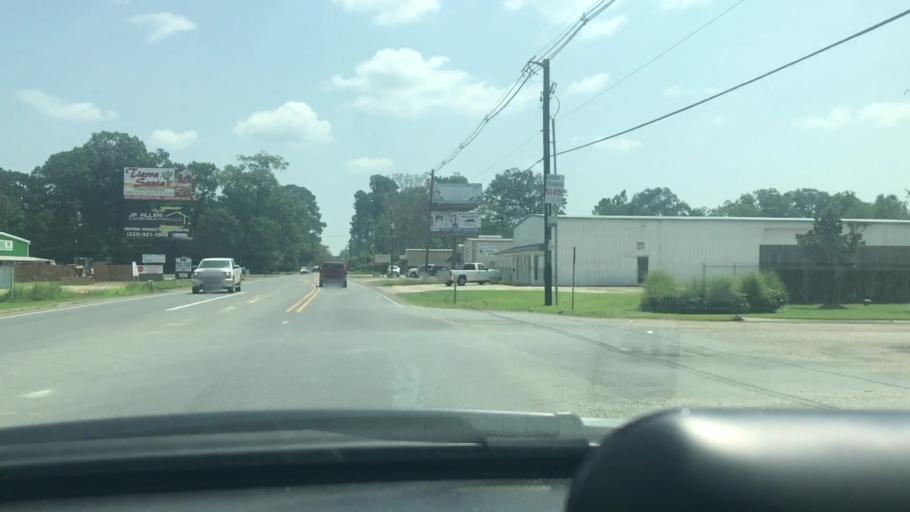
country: US
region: Louisiana
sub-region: Livingston Parish
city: Denham Springs
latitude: 30.4840
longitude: -90.9363
